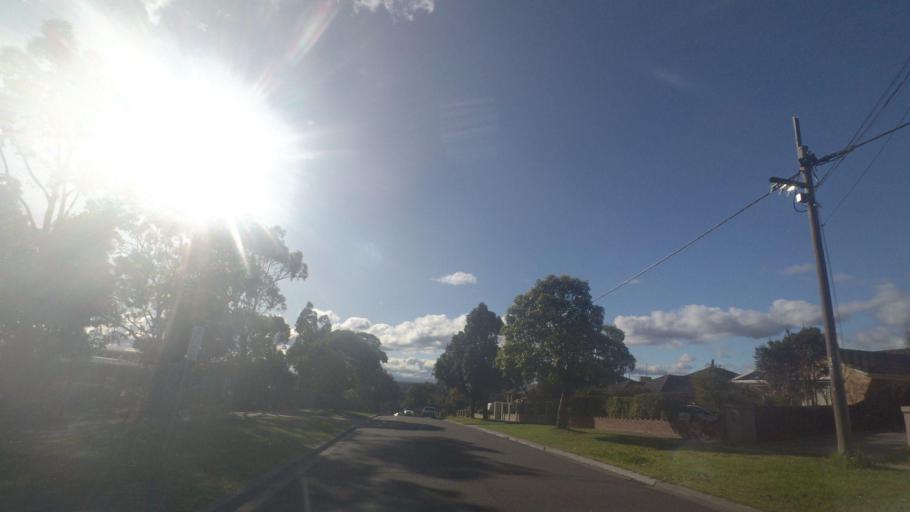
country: AU
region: Victoria
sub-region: Boroondara
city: Balwyn North
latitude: -37.7895
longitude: 145.0882
